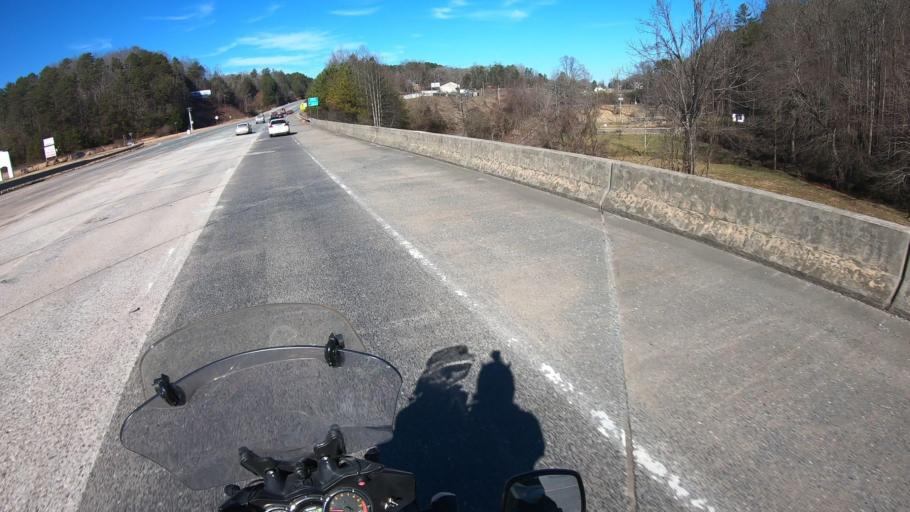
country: US
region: Georgia
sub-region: Fannin County
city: Blue Ridge
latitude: 34.8494
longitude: -84.3330
